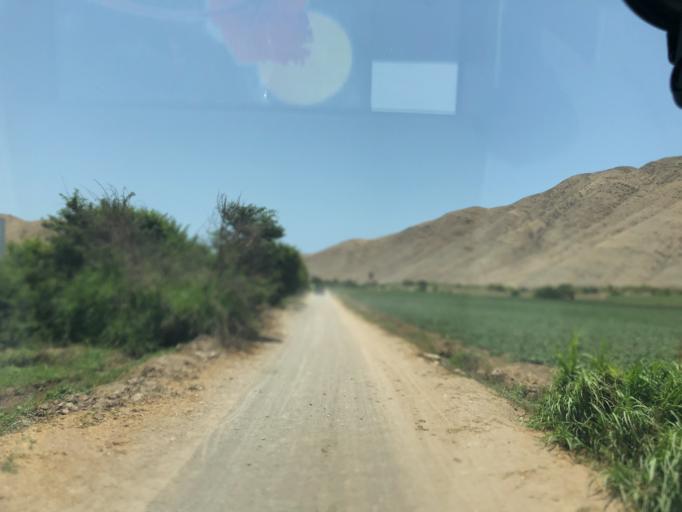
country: PE
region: Lima
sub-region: Provincia de Canete
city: Quilmana
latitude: -12.9728
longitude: -76.4211
